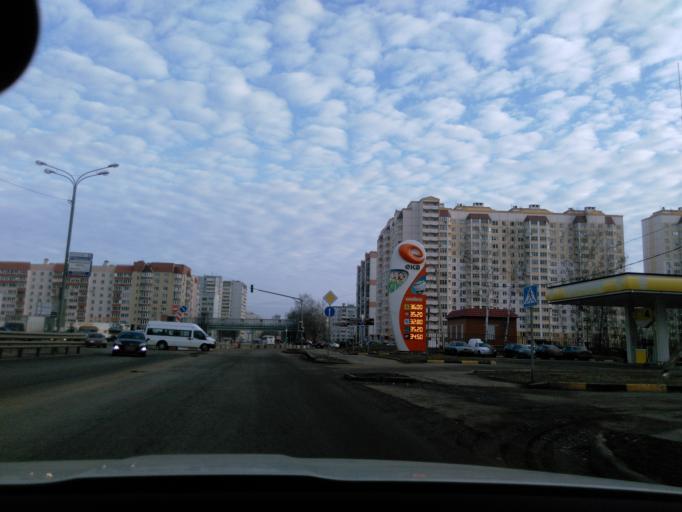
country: RU
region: Moskovskaya
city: Dolgoprudnyy
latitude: 55.9369
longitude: 37.4922
